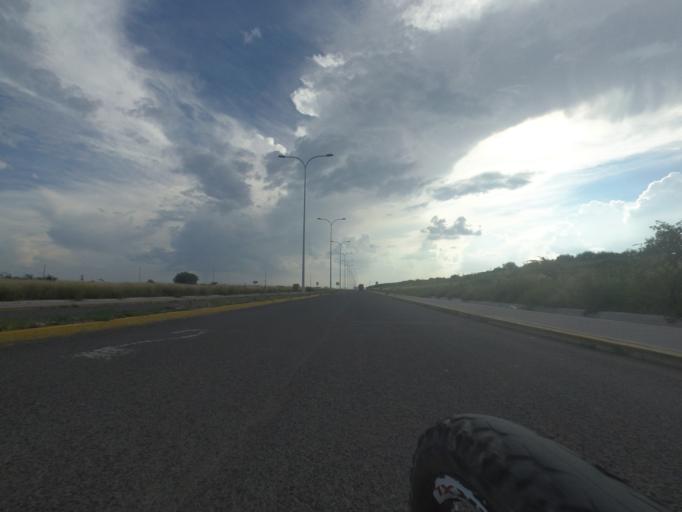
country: MX
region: Aguascalientes
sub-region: Aguascalientes
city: Penuelas (El Cienegal)
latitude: 21.7295
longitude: -102.2840
